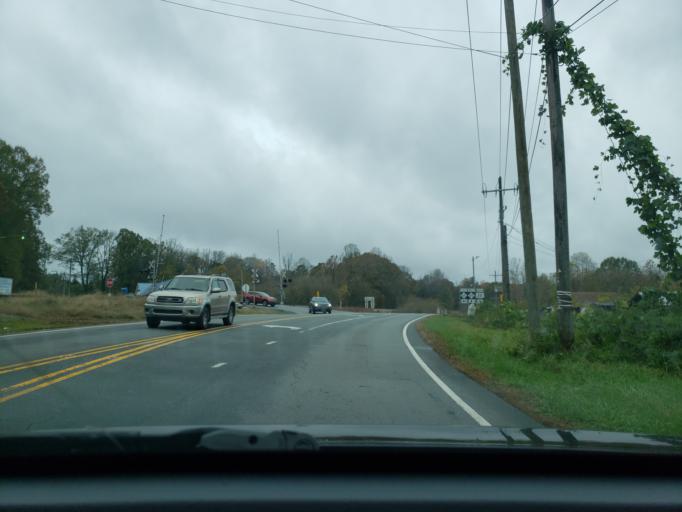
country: US
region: North Carolina
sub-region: Stokes County
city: Walnut Cove
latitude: 36.2896
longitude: -80.1410
